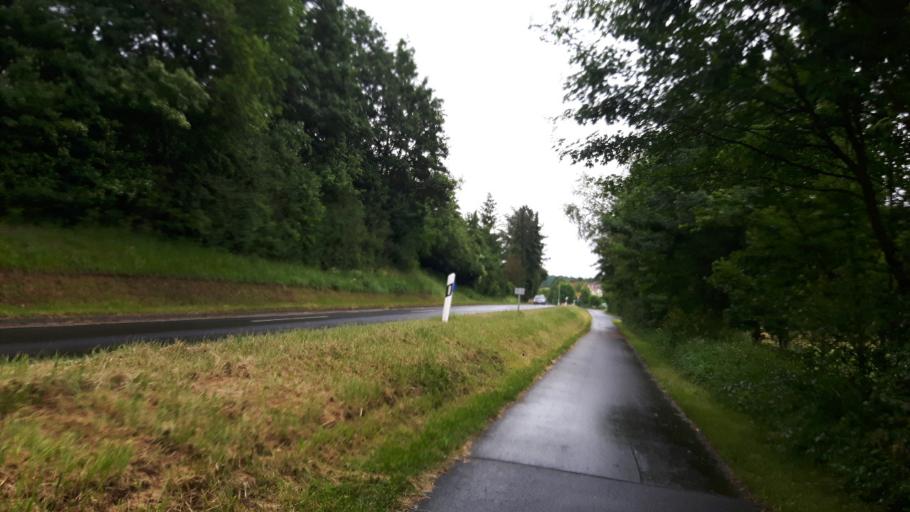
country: DE
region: Bavaria
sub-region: Regierungsbezirk Unterfranken
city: Uchtelhausen
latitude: 50.0901
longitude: 10.2477
